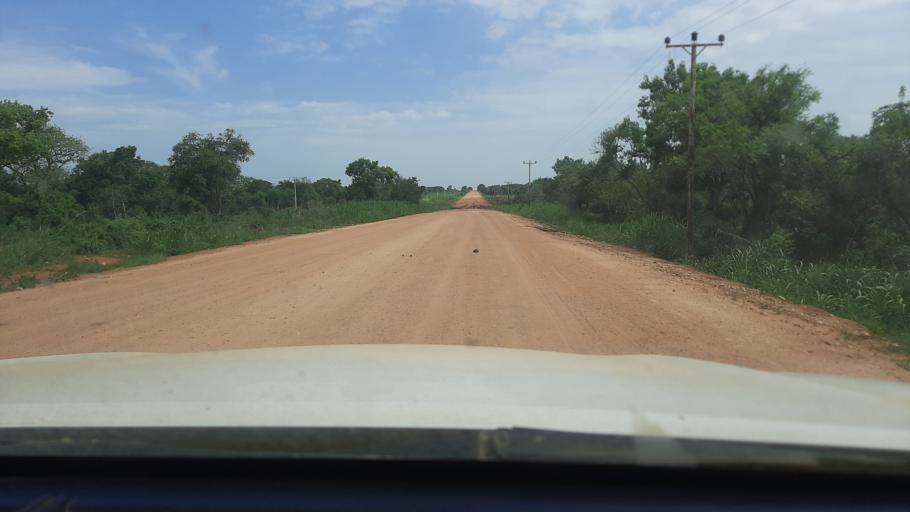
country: ET
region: Gambela
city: Gambela
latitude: 8.0210
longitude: 34.5735
